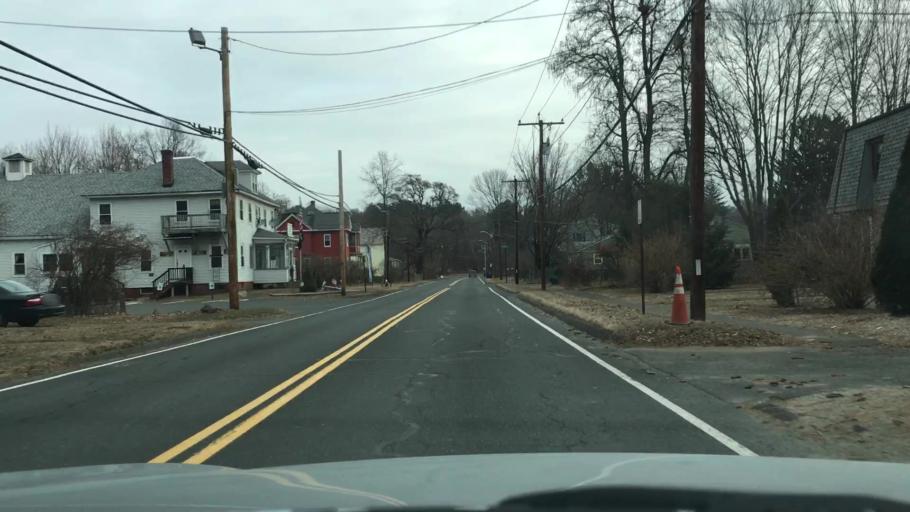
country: US
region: Massachusetts
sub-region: Hampshire County
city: Northampton
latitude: 42.3250
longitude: -72.6557
